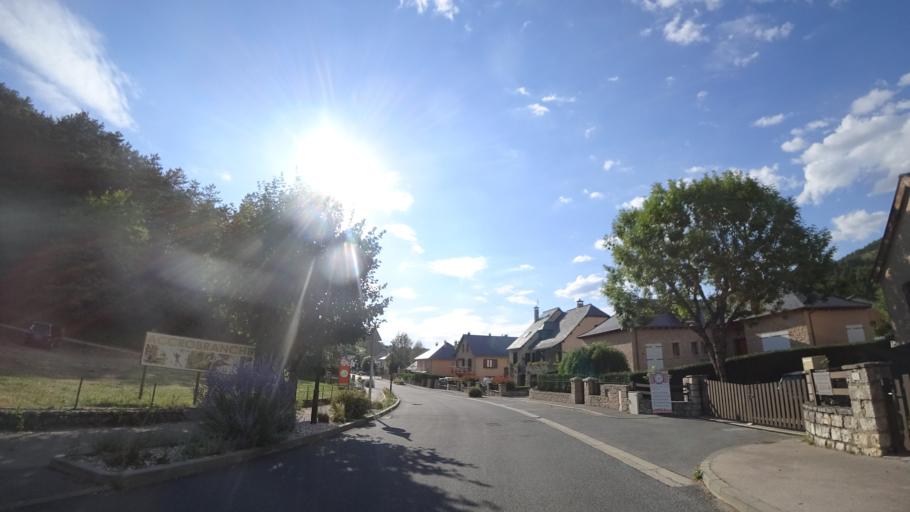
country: FR
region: Languedoc-Roussillon
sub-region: Departement de la Lozere
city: La Canourgue
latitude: 44.4289
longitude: 3.2218
